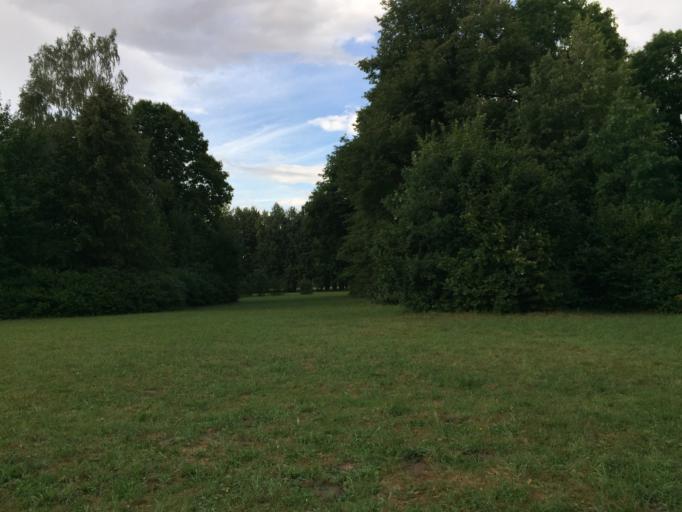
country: LT
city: Zagare
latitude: 56.3601
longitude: 23.2739
